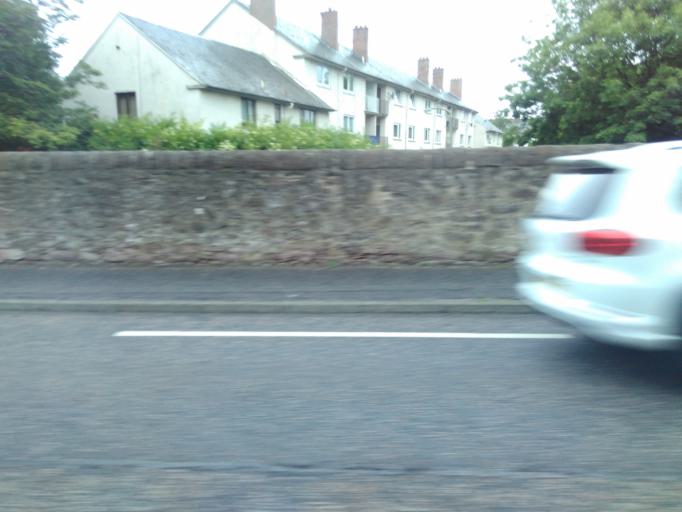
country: GB
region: Scotland
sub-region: Midlothian
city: Loanhead
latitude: 55.9202
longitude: -3.1594
